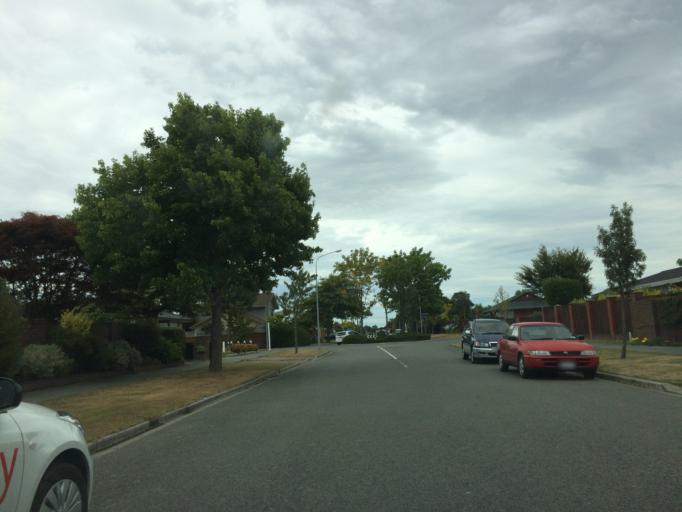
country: NZ
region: Canterbury
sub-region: Christchurch City
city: Christchurch
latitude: -43.5253
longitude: 172.5635
